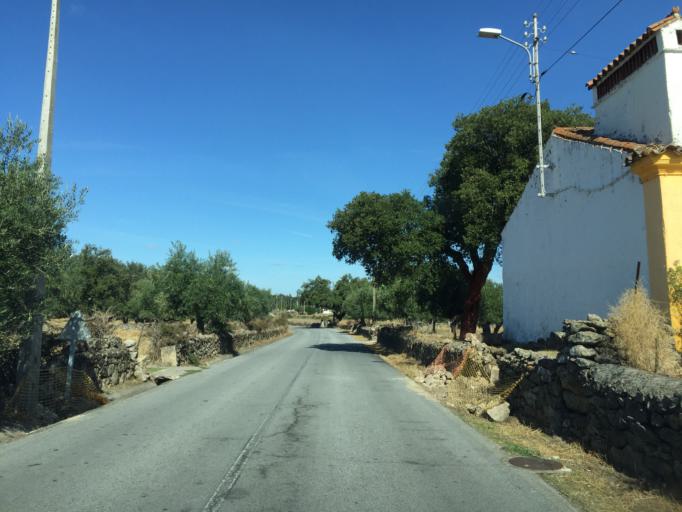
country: PT
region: Portalegre
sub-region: Marvao
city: Marvao
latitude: 39.4253
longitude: -7.3537
